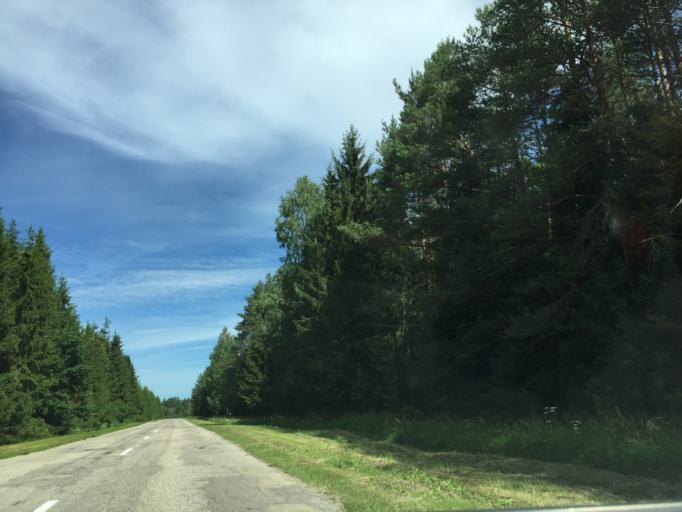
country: LV
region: Dundaga
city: Dundaga
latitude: 57.5741
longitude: 22.3057
